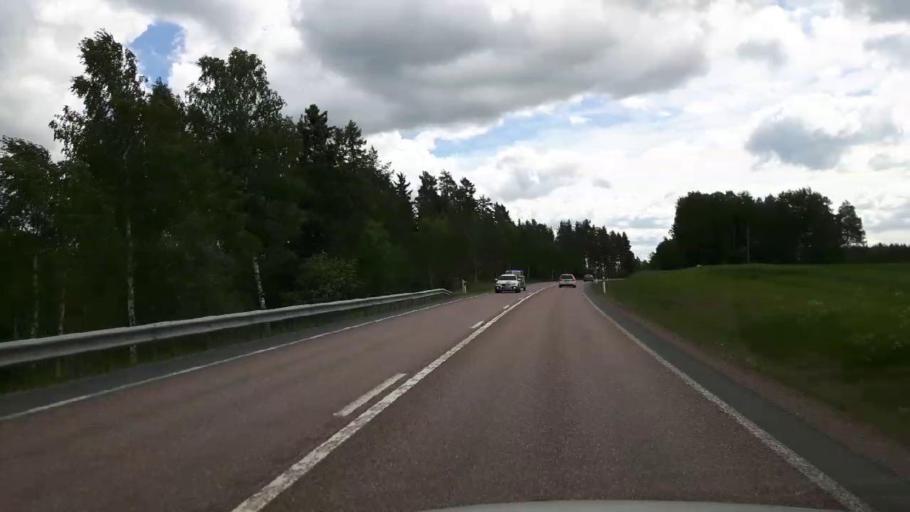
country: SE
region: Dalarna
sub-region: Saters Kommun
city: Saeter
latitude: 60.4716
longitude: 15.7946
